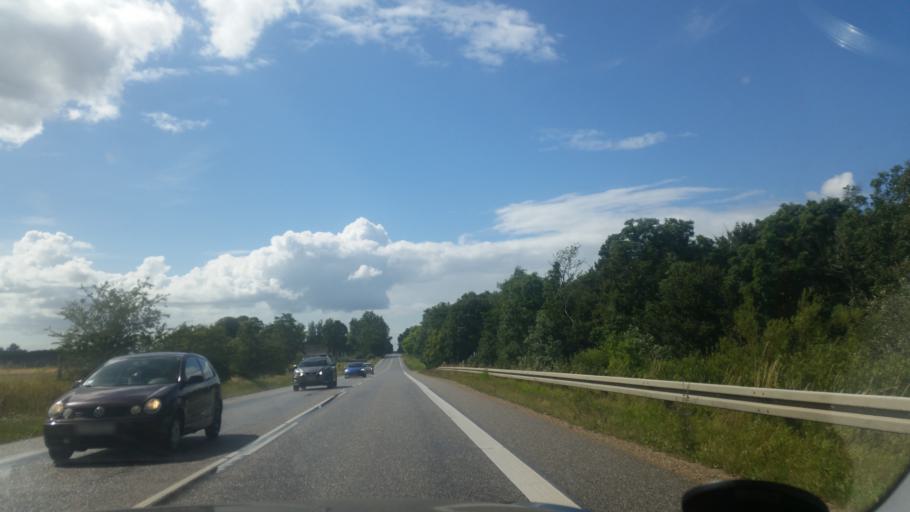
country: DK
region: Zealand
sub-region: Holbaek Kommune
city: Holbaek
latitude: 55.7190
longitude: 11.6088
